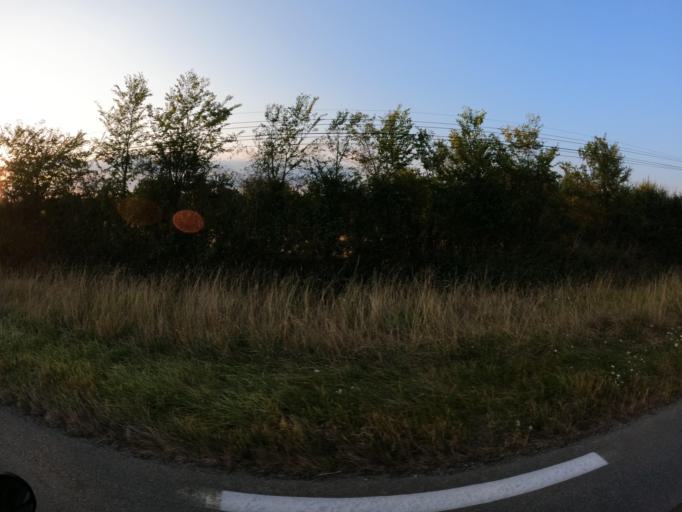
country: FR
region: Pays de la Loire
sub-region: Departement de la Mayenne
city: Meslay-du-Maine
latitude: 47.8710
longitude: -0.4805
